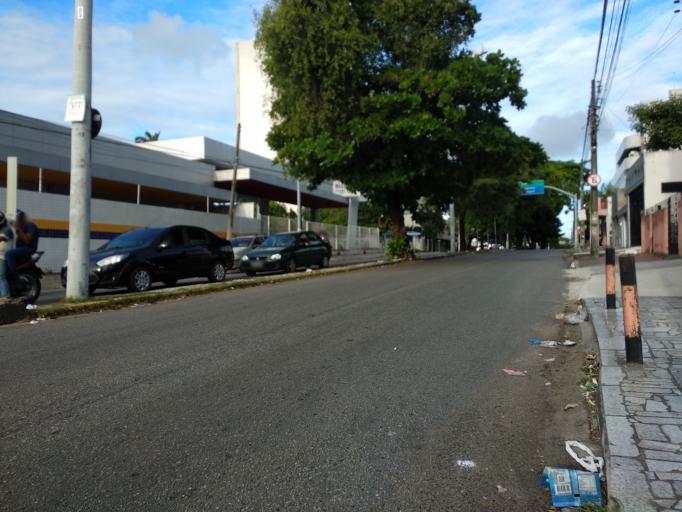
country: BR
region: Ceara
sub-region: Fortaleza
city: Fortaleza
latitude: -3.7284
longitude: -38.5402
